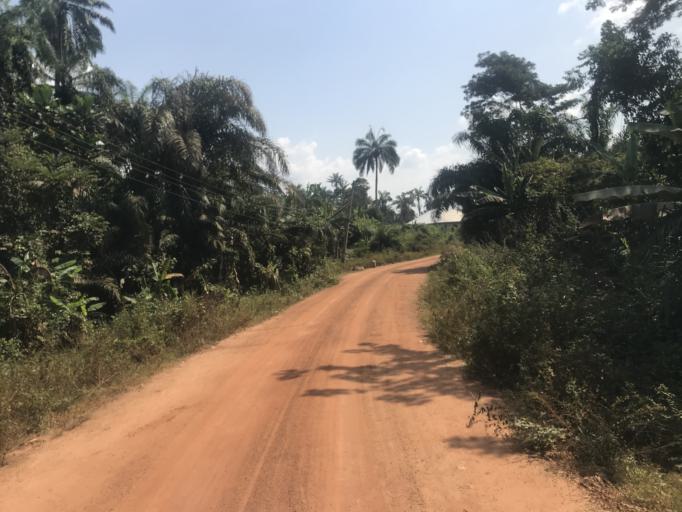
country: NG
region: Osun
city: Iragbiji
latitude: 7.8831
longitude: 4.7007
